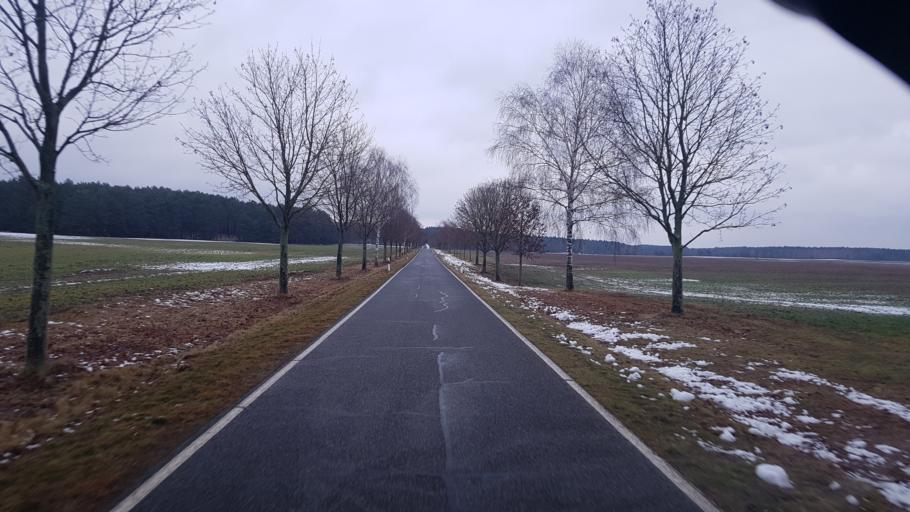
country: DE
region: Brandenburg
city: Jamlitz
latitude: 52.0183
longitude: 14.4274
